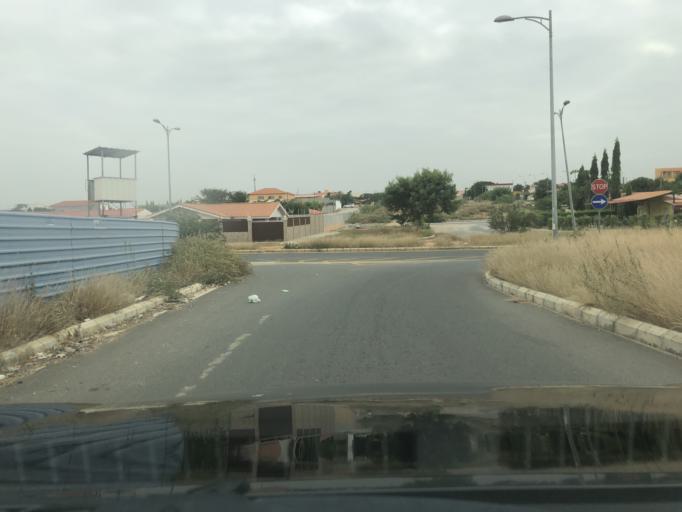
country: AO
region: Luanda
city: Luanda
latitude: -8.9459
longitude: 13.2493
